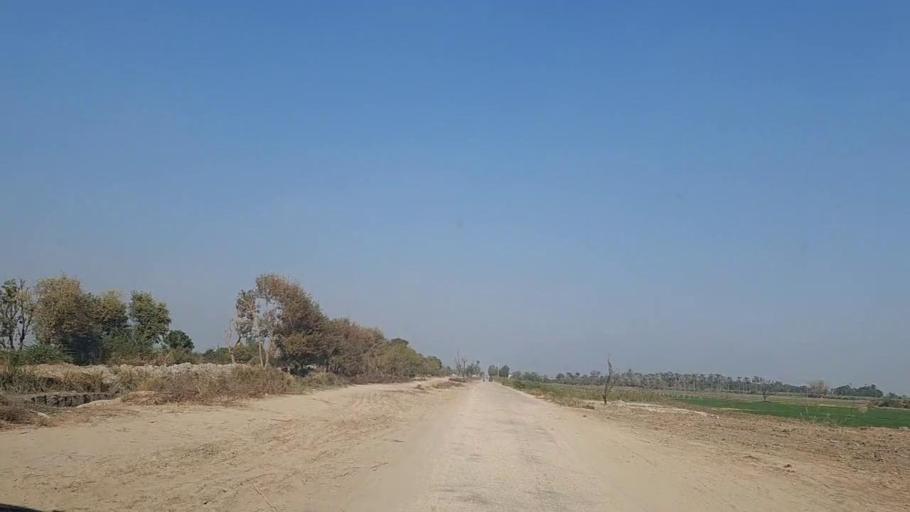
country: PK
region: Sindh
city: Sakrand
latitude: 26.0468
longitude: 68.3364
